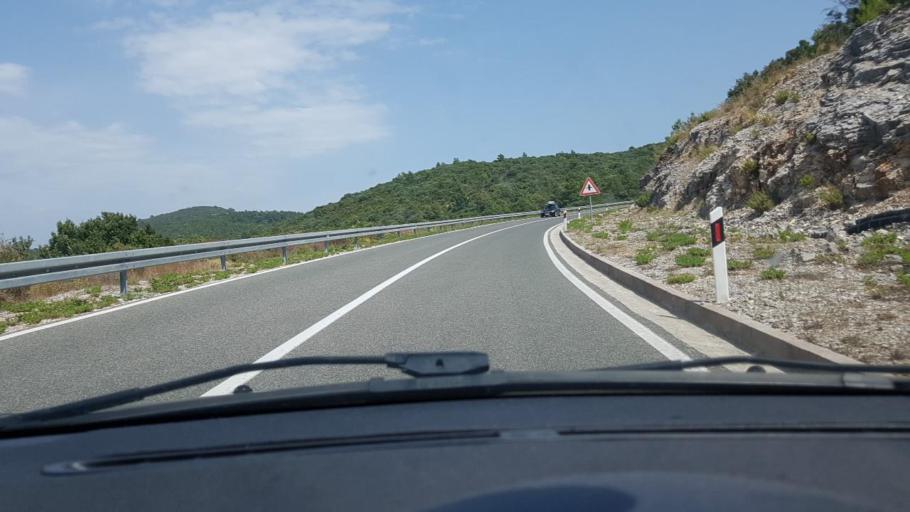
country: HR
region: Dubrovacko-Neretvanska
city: Smokvica
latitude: 42.9569
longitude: 16.9399
